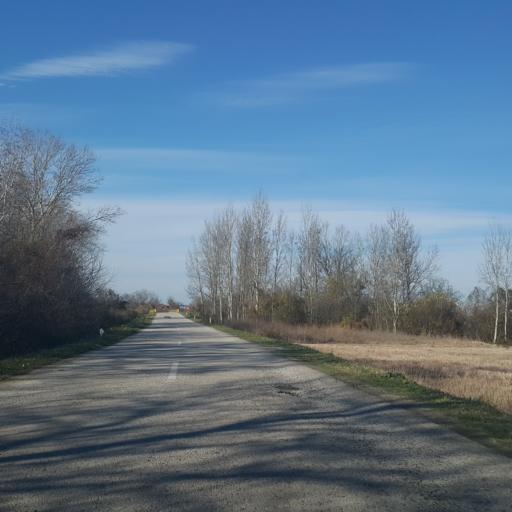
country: RS
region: Central Serbia
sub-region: Sumadijski Okrug
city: Topola
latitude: 44.2559
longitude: 20.8268
